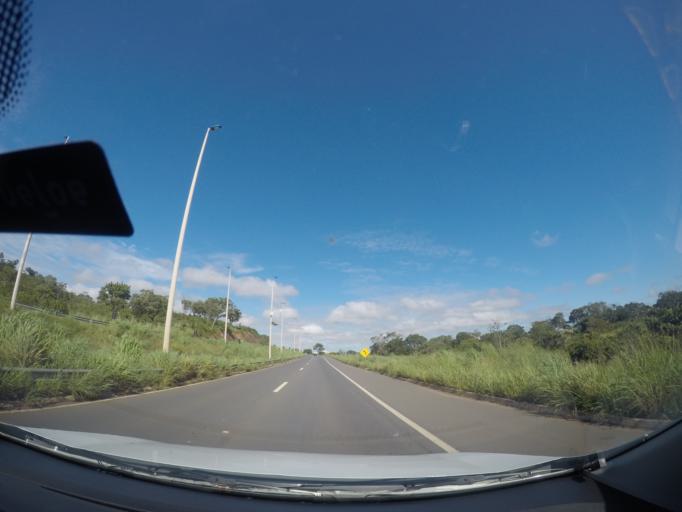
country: BR
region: Goias
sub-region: Senador Canedo
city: Senador Canedo
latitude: -16.6831
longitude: -49.1331
